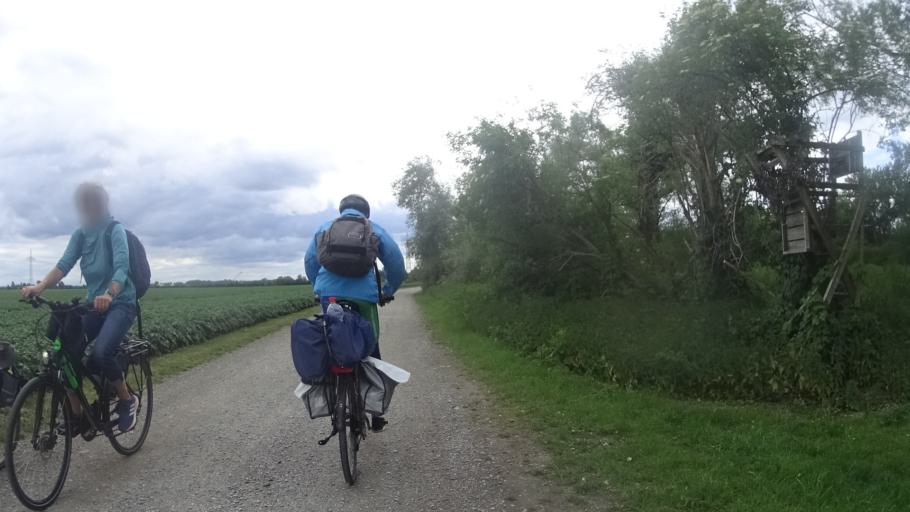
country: DE
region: Bavaria
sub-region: Upper Bavaria
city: Bergkirchen
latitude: 48.2366
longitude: 11.3676
